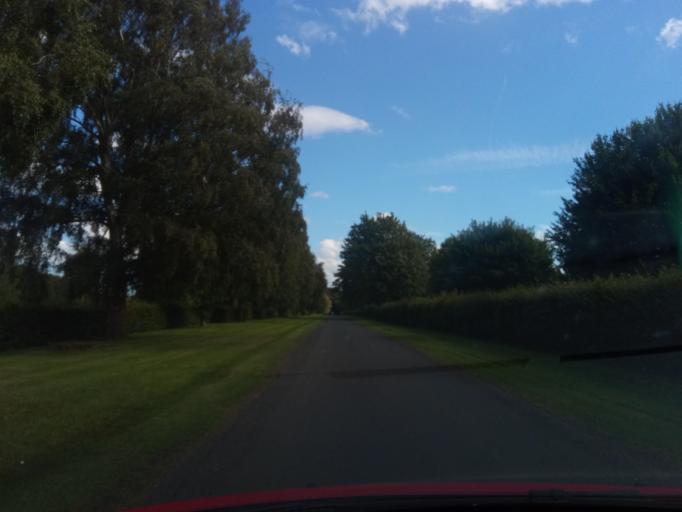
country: GB
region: Scotland
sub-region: The Scottish Borders
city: Coldstream
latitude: 55.6514
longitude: -2.2693
